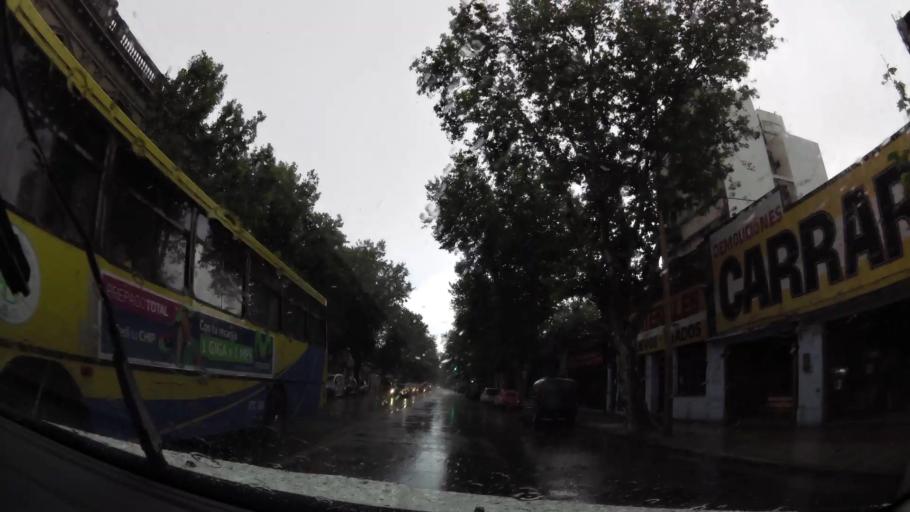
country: UY
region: Montevideo
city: Montevideo
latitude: -34.8848
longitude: -56.1840
